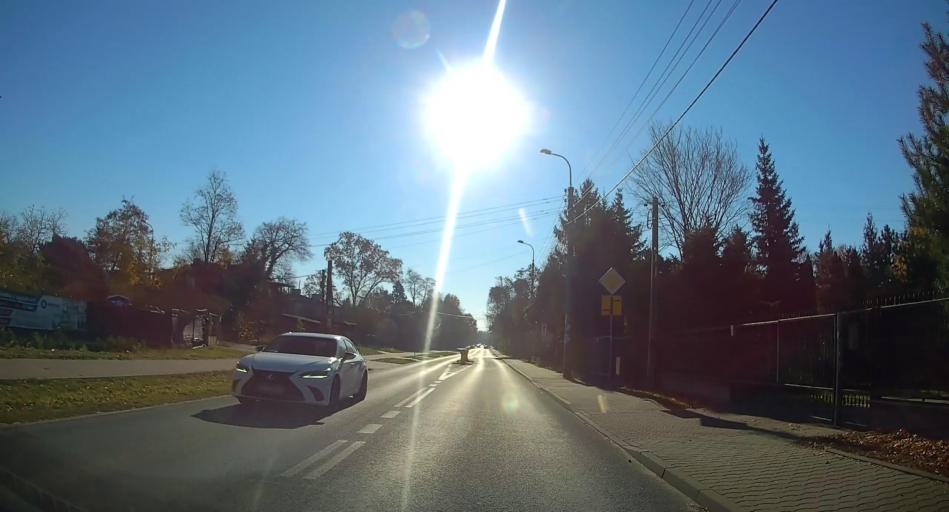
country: PL
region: Masovian Voivodeship
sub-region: Warszawa
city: Wawer
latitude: 52.2026
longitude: 21.1668
